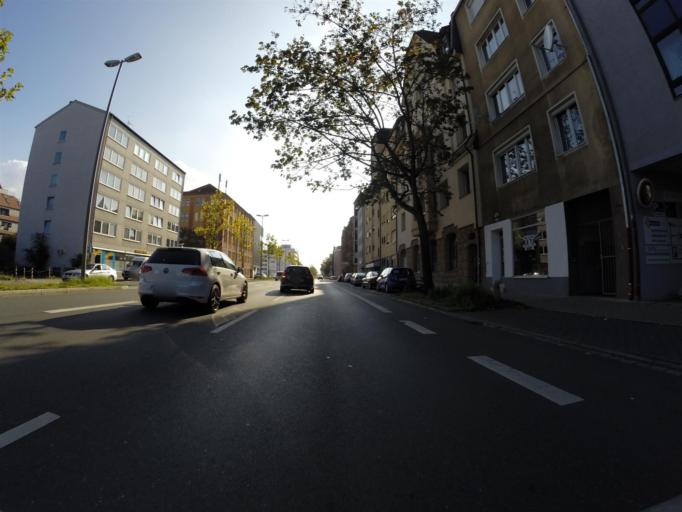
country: DE
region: Bavaria
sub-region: Regierungsbezirk Mittelfranken
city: Nuernberg
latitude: 49.4679
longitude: 11.0987
